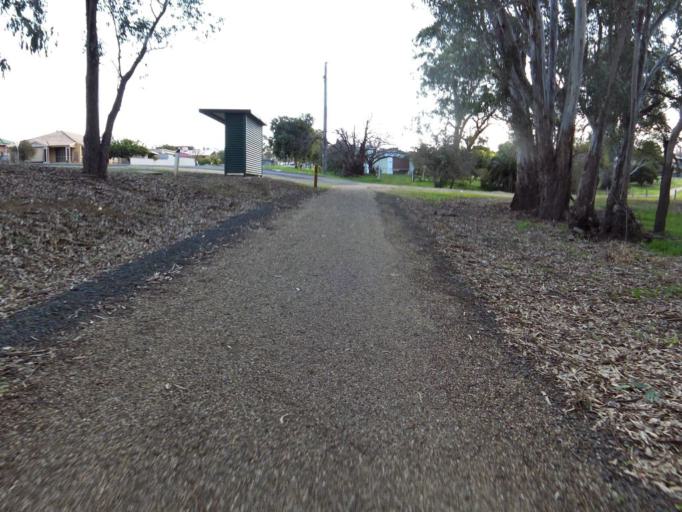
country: AU
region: New South Wales
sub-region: Corowa Shire
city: Corowa
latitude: -36.0096
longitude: 146.3970
